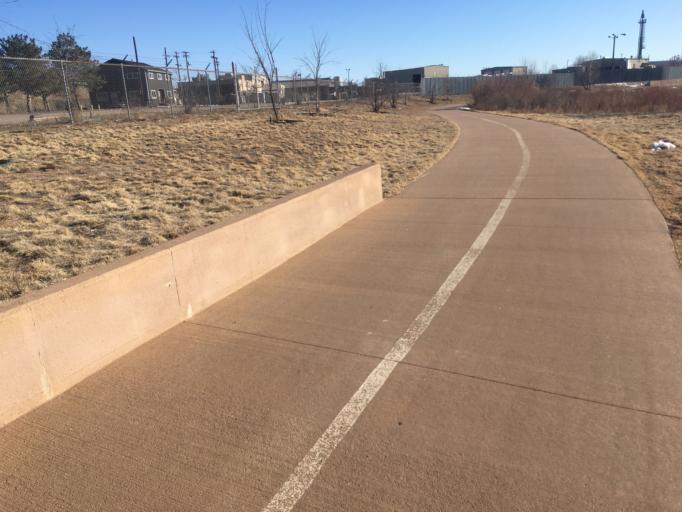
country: US
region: Colorado
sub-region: Adams County
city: Commerce City
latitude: 39.8042
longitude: -104.9404
